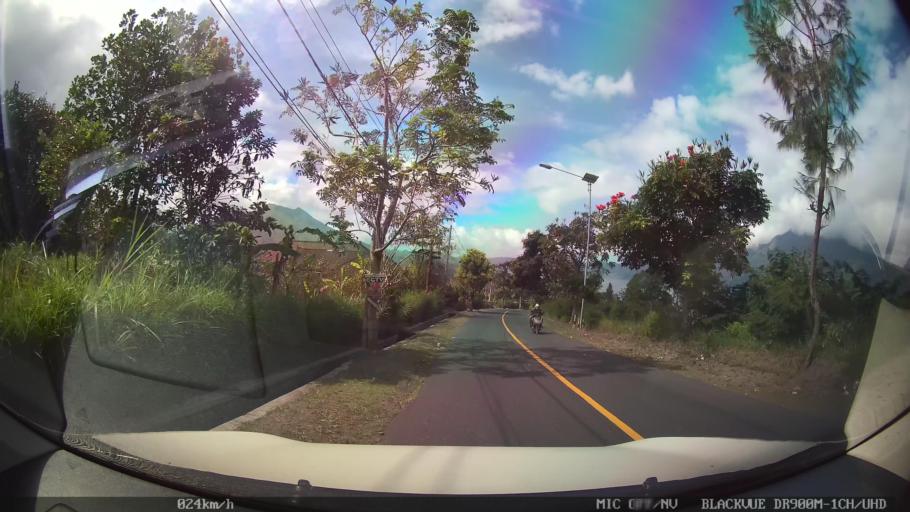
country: ID
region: Bali
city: Banjar Kedisan
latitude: -8.2810
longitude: 115.3666
